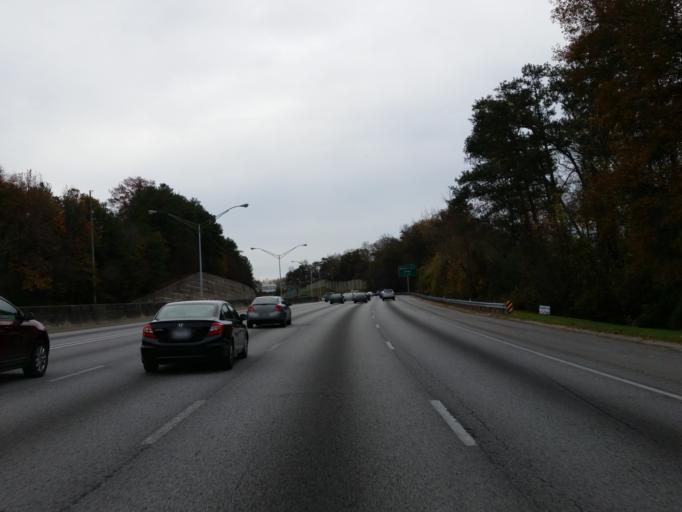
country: US
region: Georgia
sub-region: Cobb County
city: Vinings
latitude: 33.8438
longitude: -84.4299
